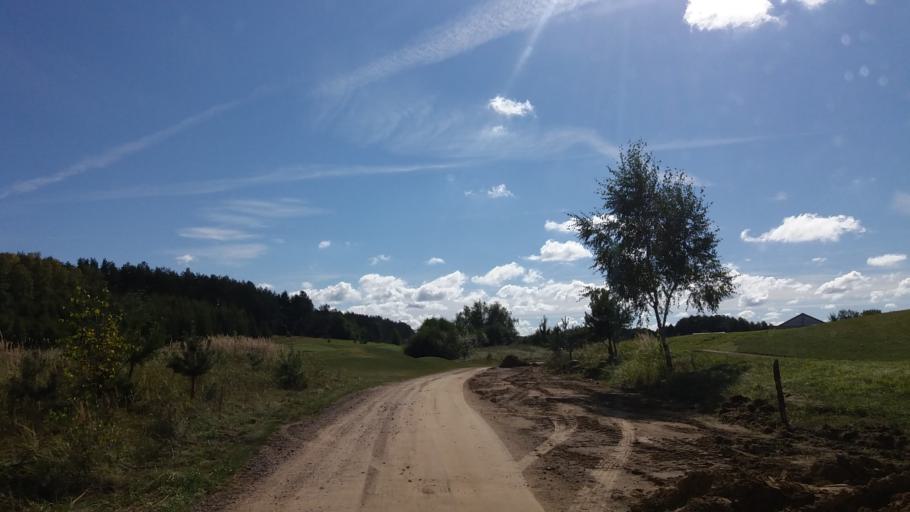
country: PL
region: West Pomeranian Voivodeship
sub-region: Powiat choszczenski
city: Krzecin
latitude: 53.1340
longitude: 15.4865
